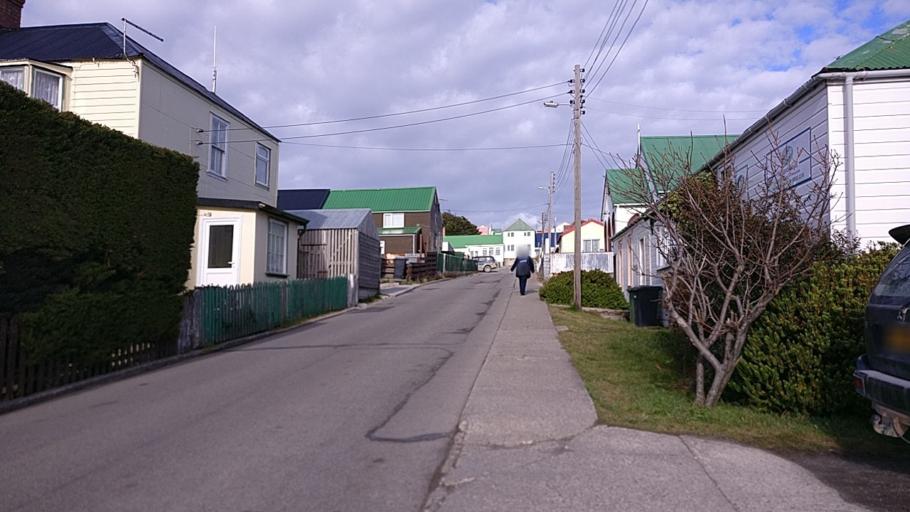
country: FK
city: Stanley
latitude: -51.6918
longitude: -57.8646
